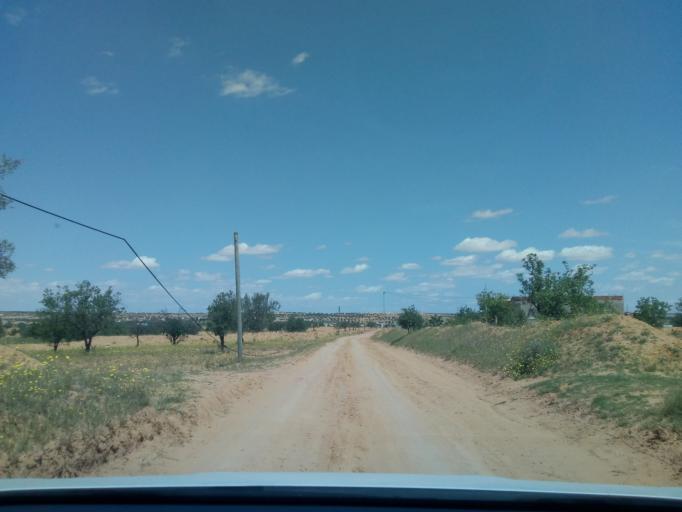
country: TN
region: Safaqis
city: Sfax
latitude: 34.7297
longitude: 10.4868
